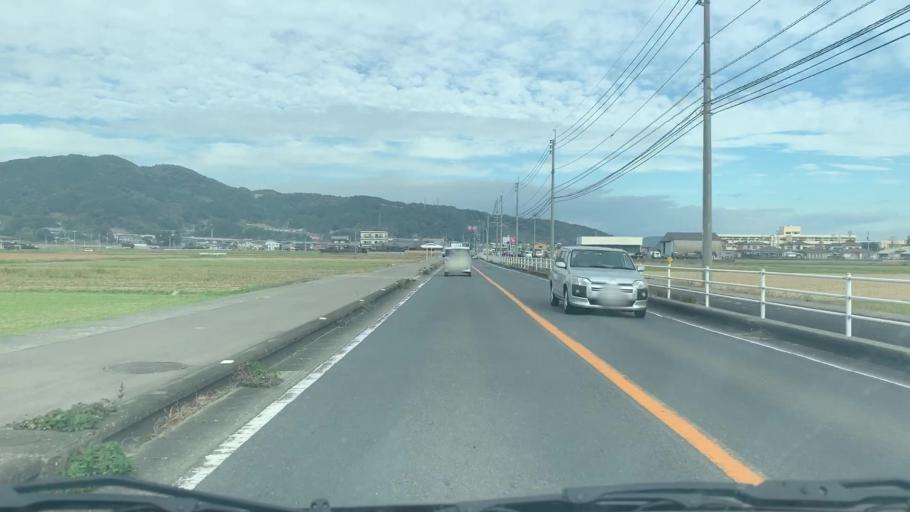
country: JP
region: Saga Prefecture
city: Karatsu
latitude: 33.4011
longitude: 129.9871
